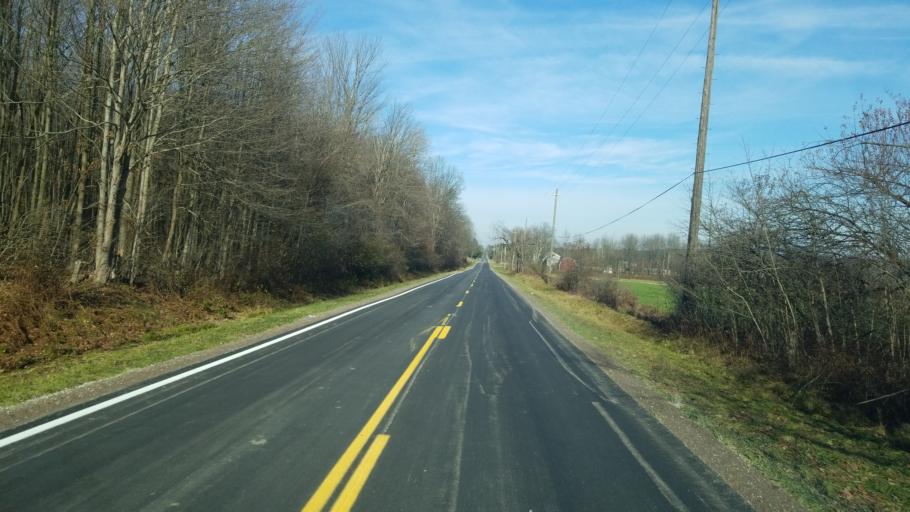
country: US
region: Ohio
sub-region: Ashtabula County
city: Roaming Shores
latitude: 41.7054
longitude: -80.9039
